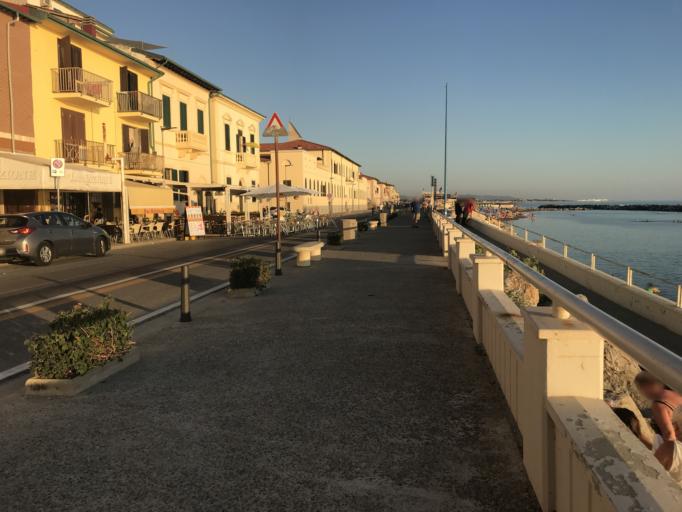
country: IT
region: Tuscany
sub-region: Province of Pisa
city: Marina di Pisa
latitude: 43.6622
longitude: 10.2782
